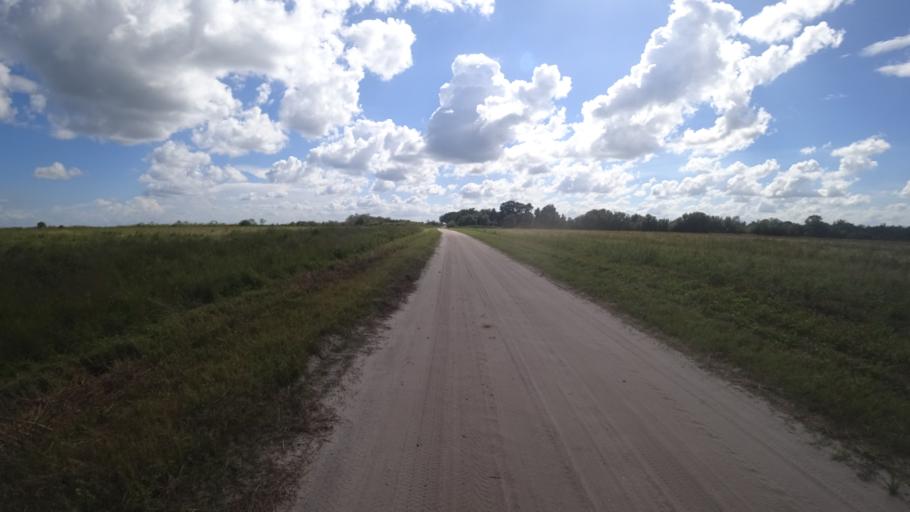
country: US
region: Florida
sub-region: DeSoto County
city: Arcadia
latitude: 27.3406
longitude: -82.1050
